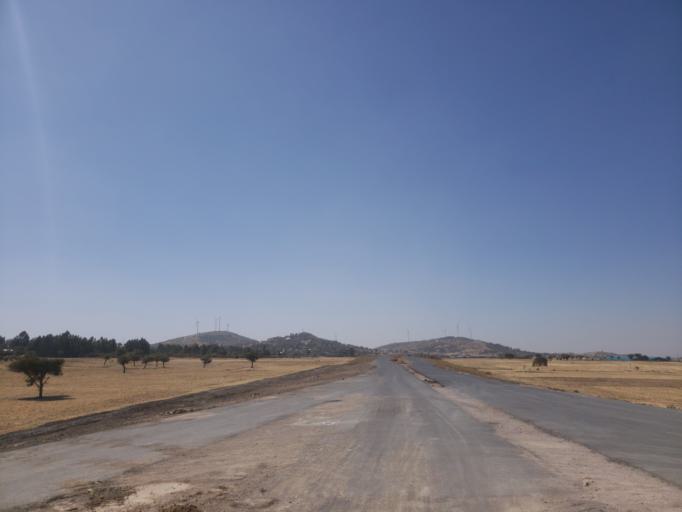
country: ET
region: Oromiya
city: Mojo
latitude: 8.5782
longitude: 39.1723
